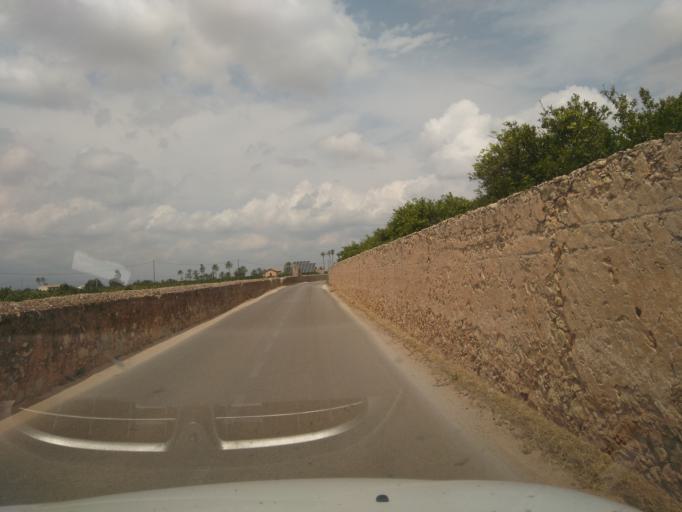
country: ES
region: Valencia
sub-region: Provincia de Valencia
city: La Pobla Llarga
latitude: 39.0991
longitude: -0.4321
